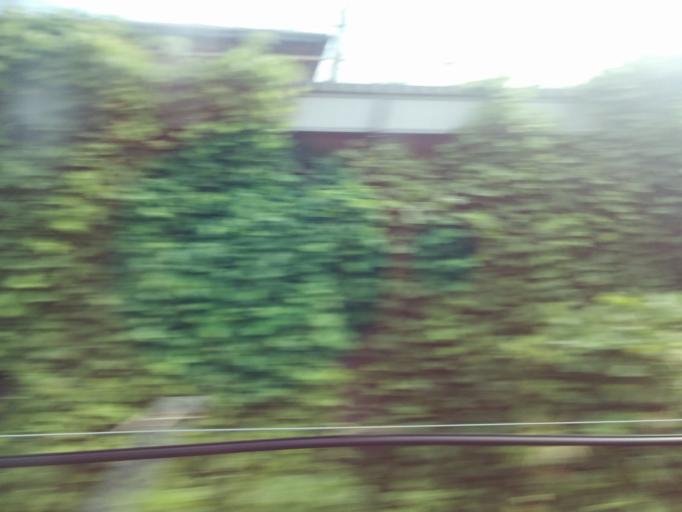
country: JP
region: Shizuoka
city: Numazu
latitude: 35.1262
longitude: 138.8404
